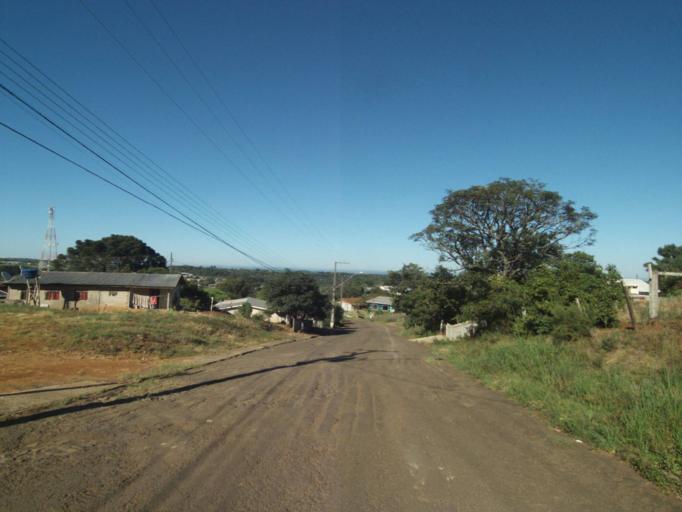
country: BR
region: Parana
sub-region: Pinhao
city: Pinhao
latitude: -25.8356
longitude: -52.0241
